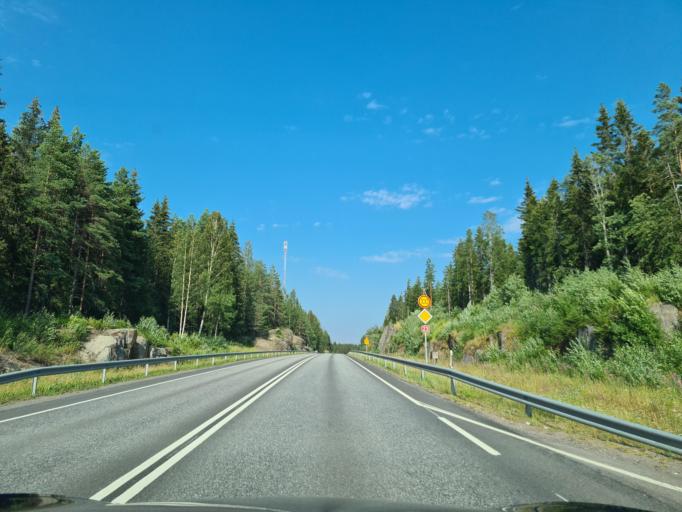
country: FI
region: Satakunta
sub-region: Pori
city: Laengelmaeki
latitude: 61.7841
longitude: 22.2157
